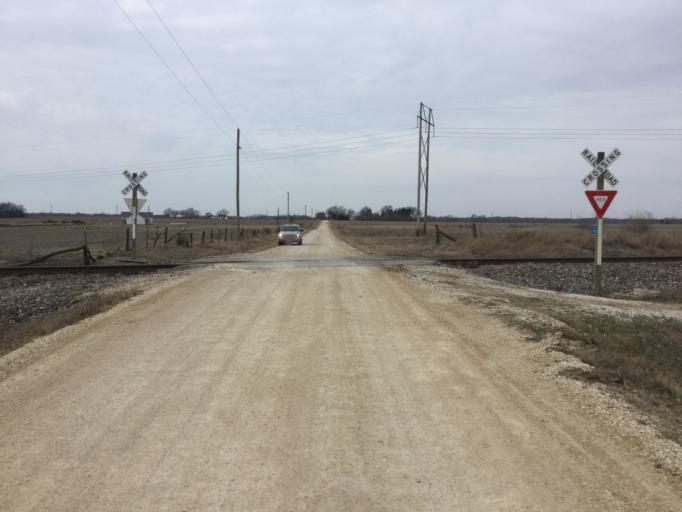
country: US
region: Kansas
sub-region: Allen County
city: Iola
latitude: 37.8489
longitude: -95.1528
